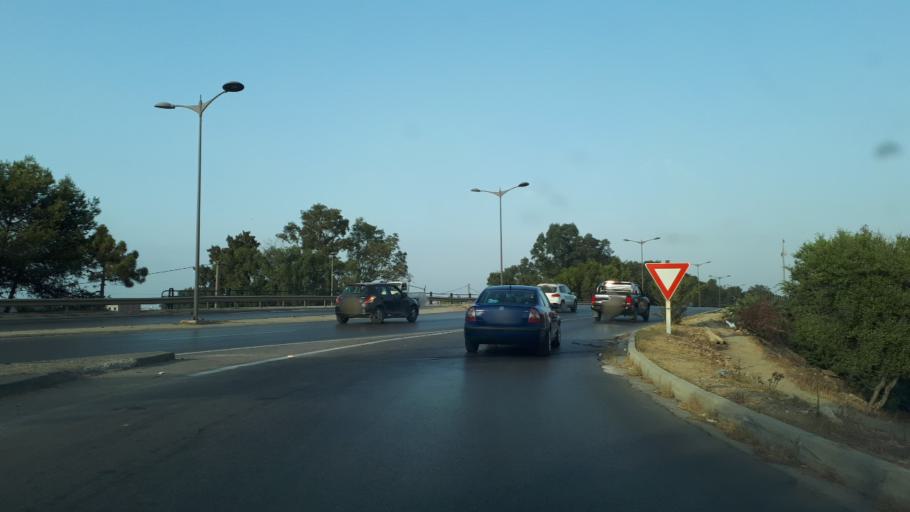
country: DZ
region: Alger
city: Dar el Beida
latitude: 36.7271
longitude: 3.2105
